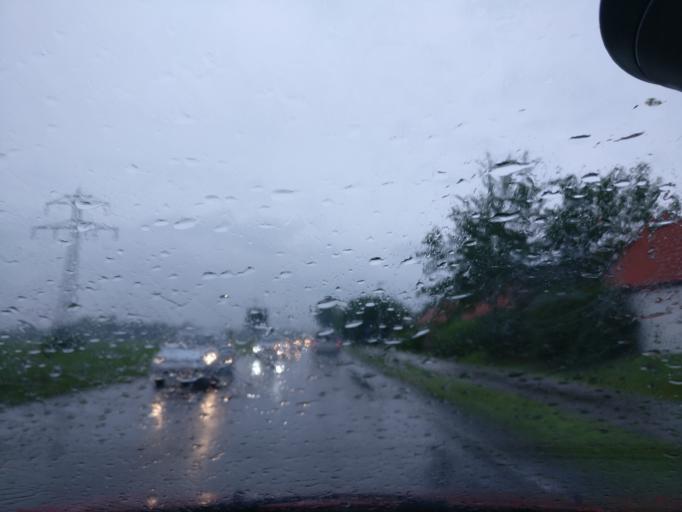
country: DE
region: Bavaria
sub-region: Upper Bavaria
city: Dachau
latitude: 48.2551
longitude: 11.4557
